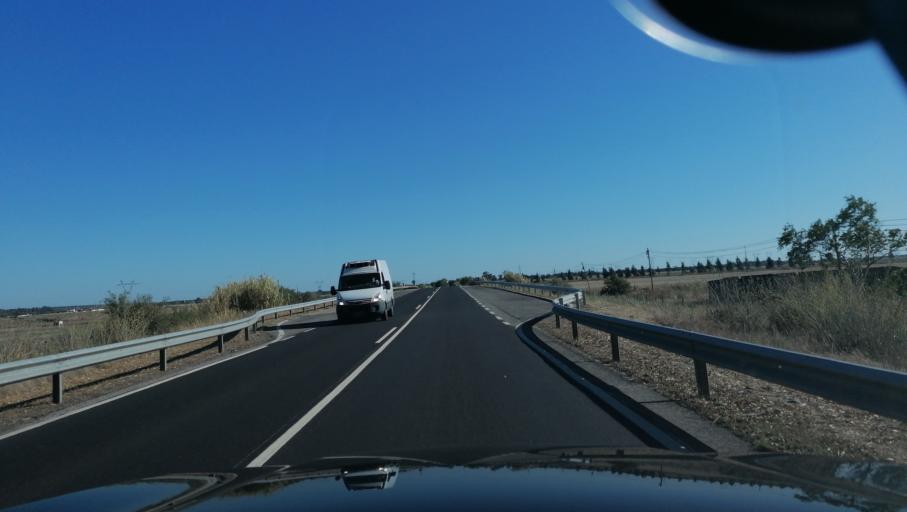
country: PT
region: Santarem
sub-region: Benavente
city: Samora Correia
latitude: 38.8879
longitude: -8.8814
